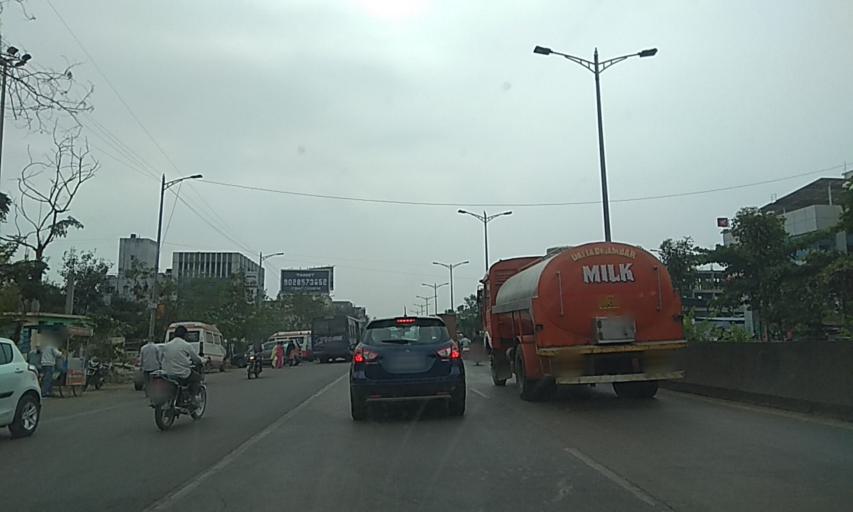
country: IN
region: Maharashtra
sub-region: Pune Division
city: Lohogaon
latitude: 18.5419
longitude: 73.9350
